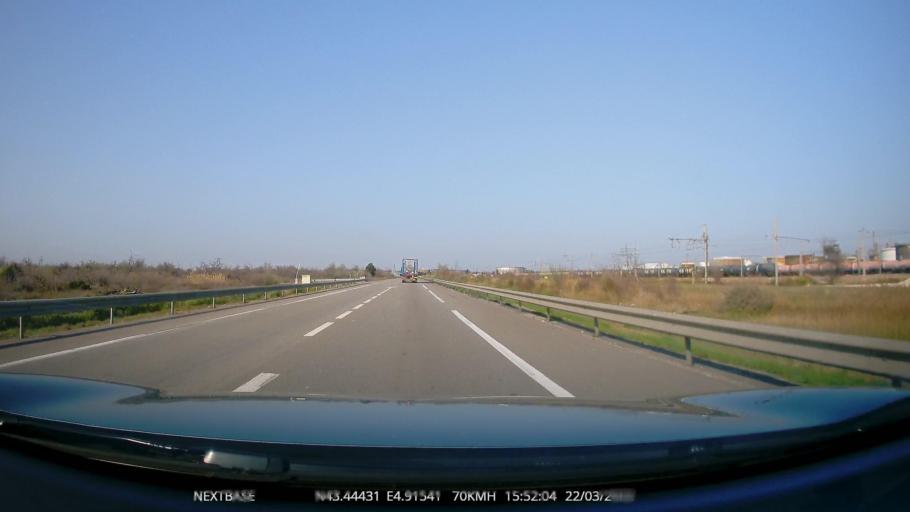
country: FR
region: Provence-Alpes-Cote d'Azur
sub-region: Departement des Bouches-du-Rhone
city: Fos-sur-Mer
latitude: 43.4430
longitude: 4.9157
